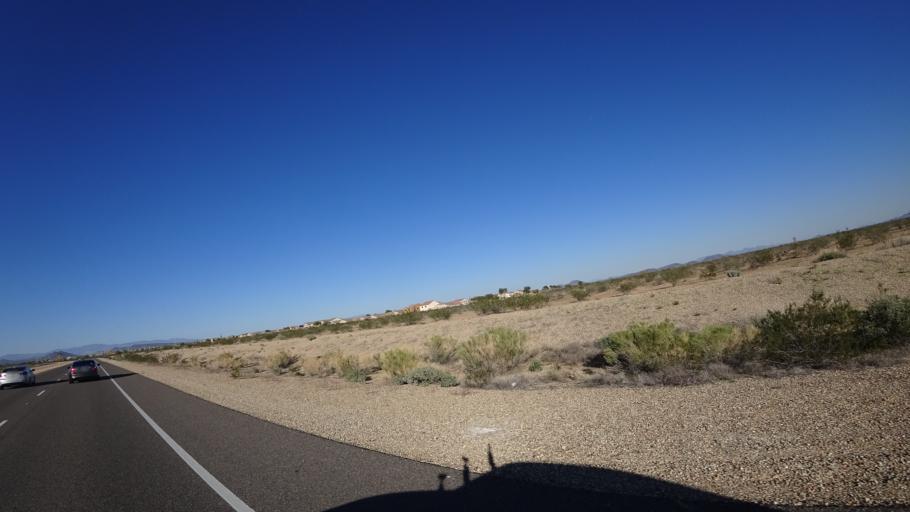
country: US
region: Arizona
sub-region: Maricopa County
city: Sun City West
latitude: 33.6770
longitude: -112.3228
